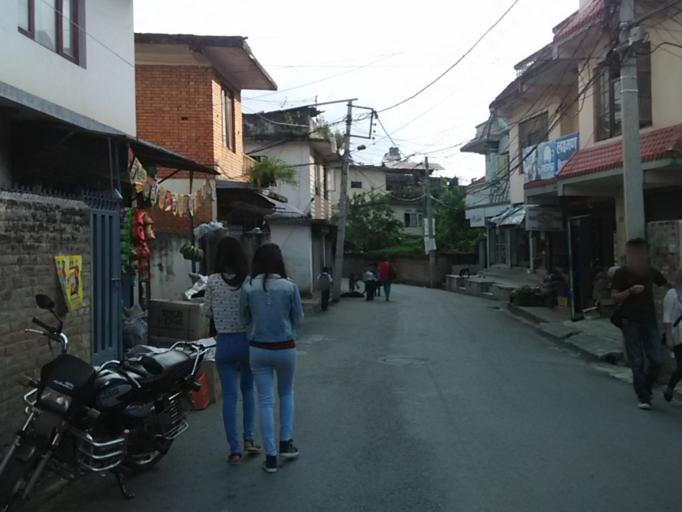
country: NP
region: Central Region
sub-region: Bagmati Zone
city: Kathmandu
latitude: 27.7258
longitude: 85.3334
